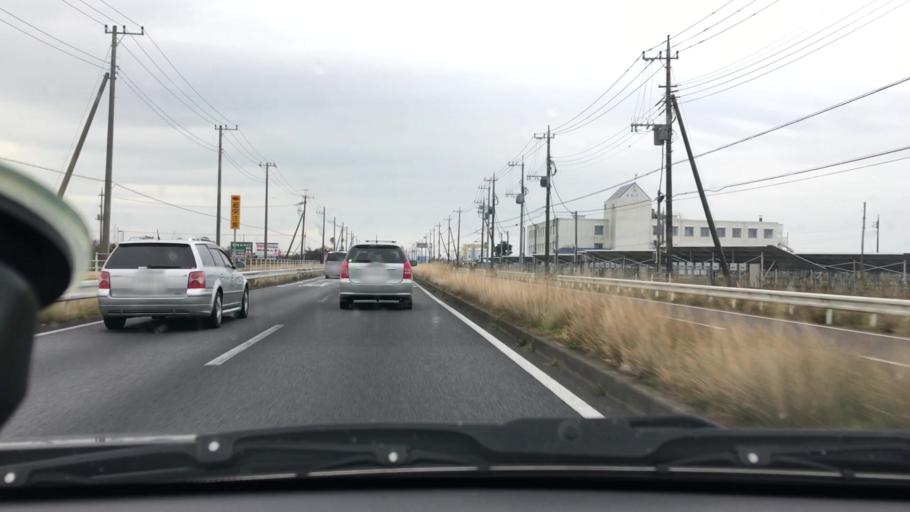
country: JP
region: Ibaraki
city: Itako
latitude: 35.9333
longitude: 140.5997
